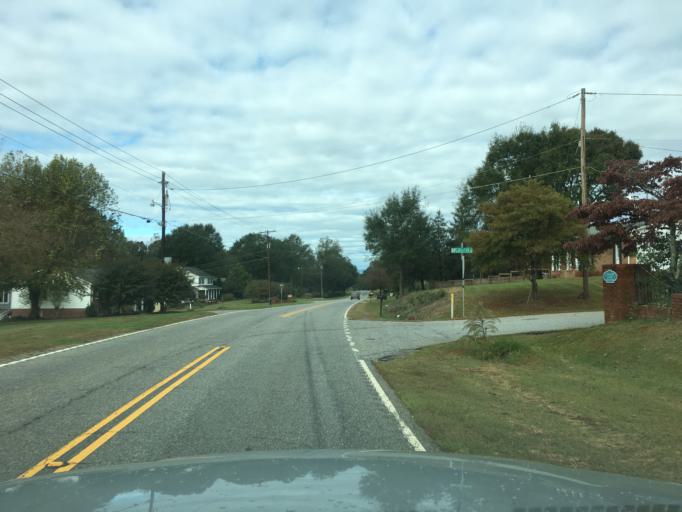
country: US
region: South Carolina
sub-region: Greenville County
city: Greer
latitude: 34.9760
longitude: -82.2071
